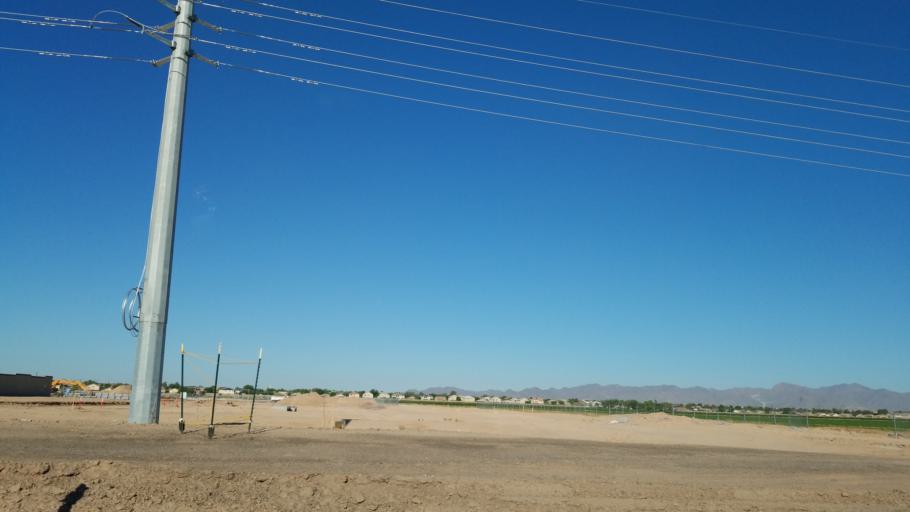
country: US
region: Arizona
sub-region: Maricopa County
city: Goodyear
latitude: 33.4429
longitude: -112.3755
